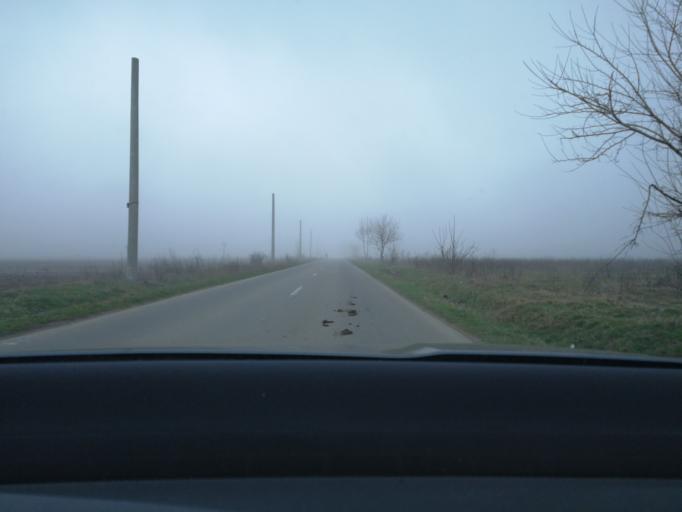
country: RO
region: Prahova
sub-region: Comuna Magureni
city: Lunca Prahovei
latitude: 45.0284
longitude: 25.7712
